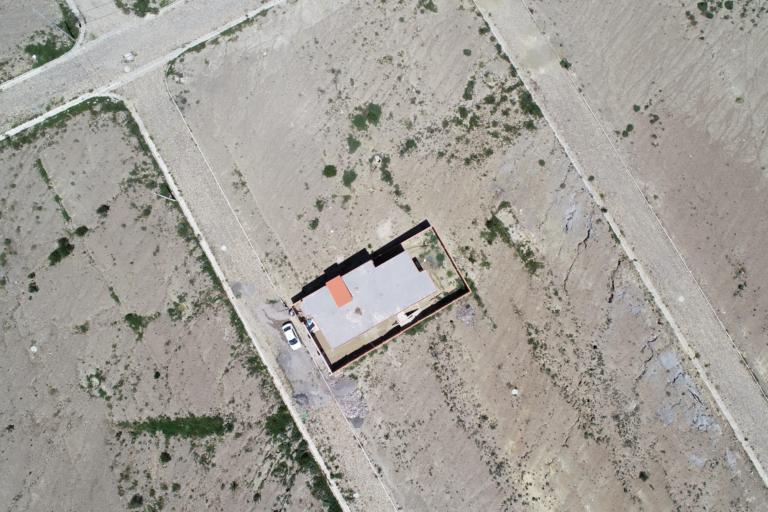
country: BO
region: La Paz
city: La Paz
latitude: -16.5224
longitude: -68.0480
